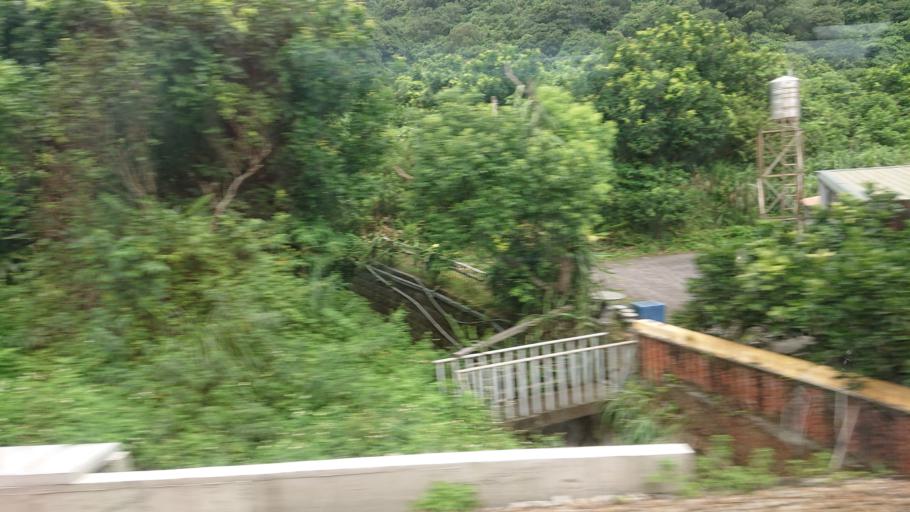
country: TW
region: Taiwan
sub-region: Yilan
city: Yilan
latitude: 24.9225
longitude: 121.8829
